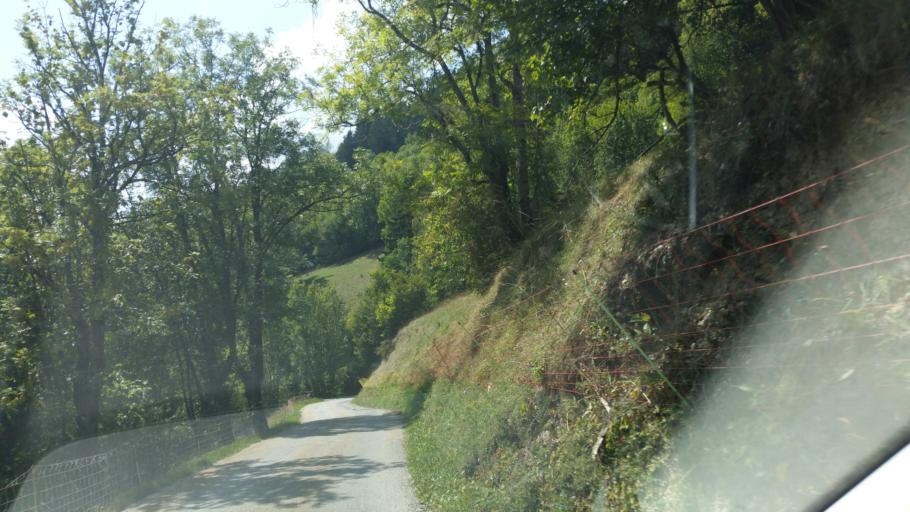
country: FR
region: Rhone-Alpes
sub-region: Departement de la Savoie
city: La Chambre
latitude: 45.3952
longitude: 6.3183
